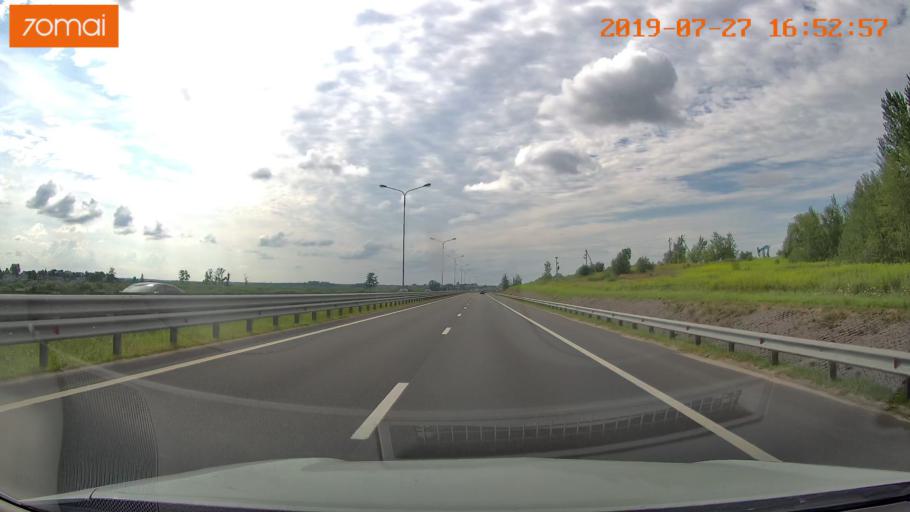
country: RU
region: Kaliningrad
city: Gvardeysk
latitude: 54.6853
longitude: 20.8426
